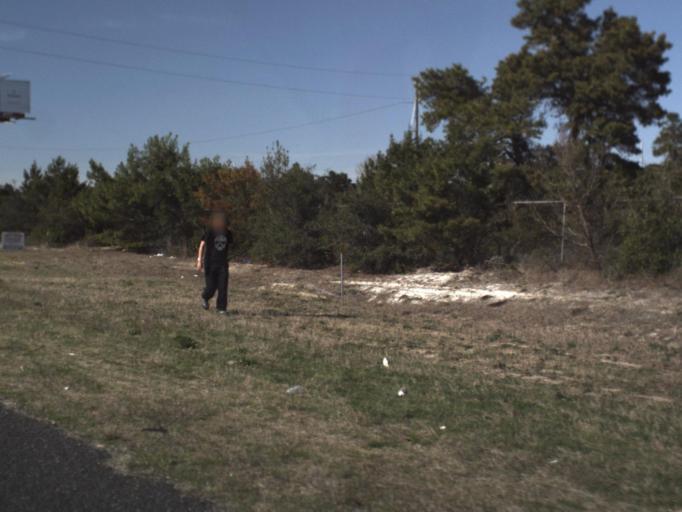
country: US
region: Florida
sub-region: Bay County
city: Laguna Beach
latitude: 30.2415
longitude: -85.9148
